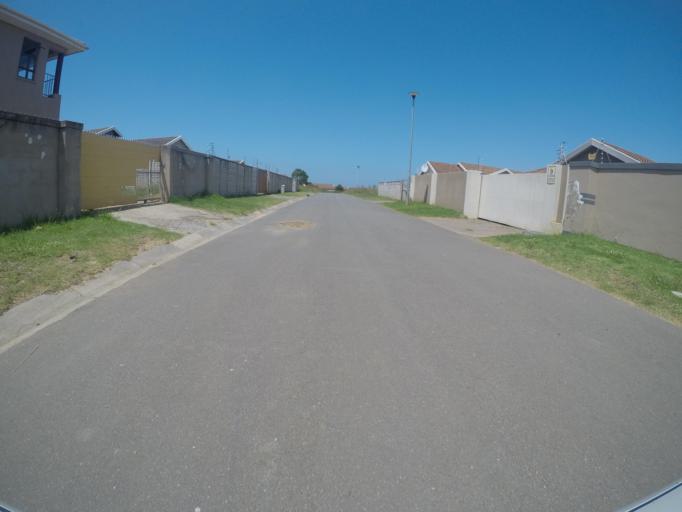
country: ZA
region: Eastern Cape
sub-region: Buffalo City Metropolitan Municipality
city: East London
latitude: -32.9407
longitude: 27.9935
